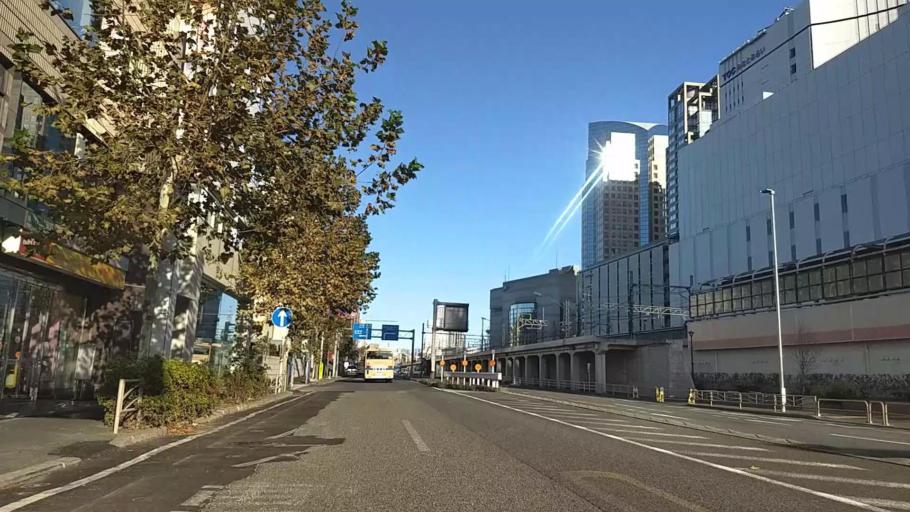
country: JP
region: Kanagawa
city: Yokohama
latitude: 35.4510
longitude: 139.6303
